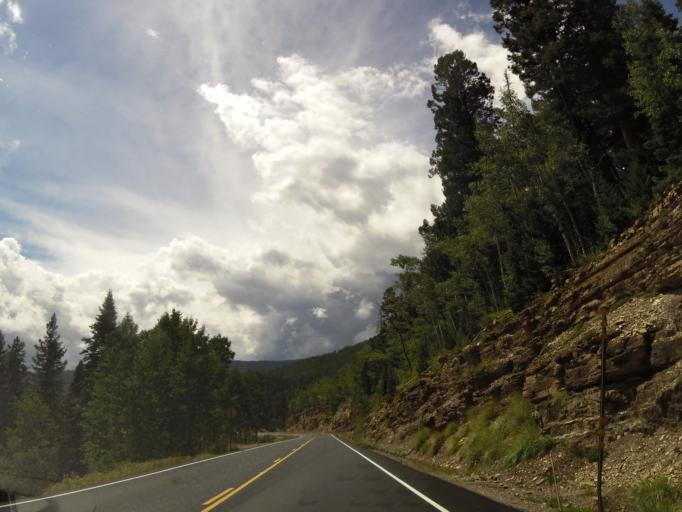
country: US
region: Colorado
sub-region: San Juan County
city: Silverton
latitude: 37.6802
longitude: -107.7898
